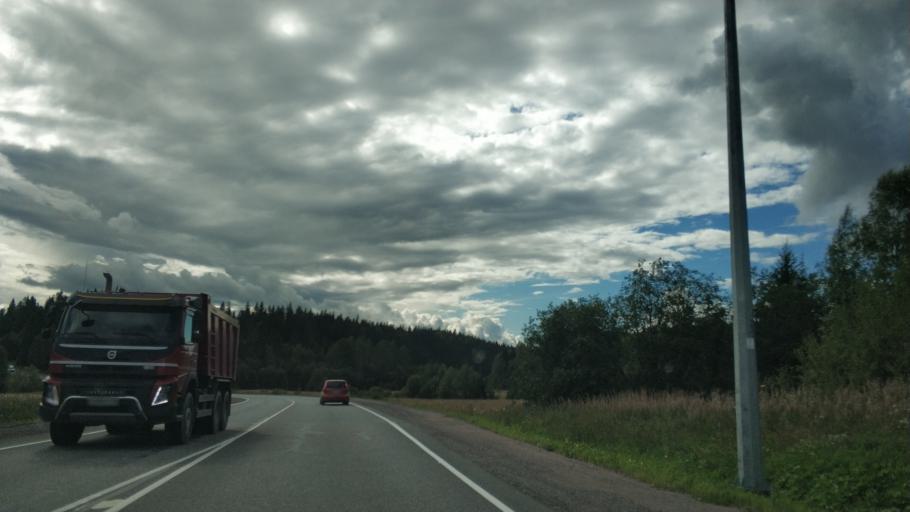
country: RU
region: Republic of Karelia
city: Khelyulya
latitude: 61.7744
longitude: 30.6585
